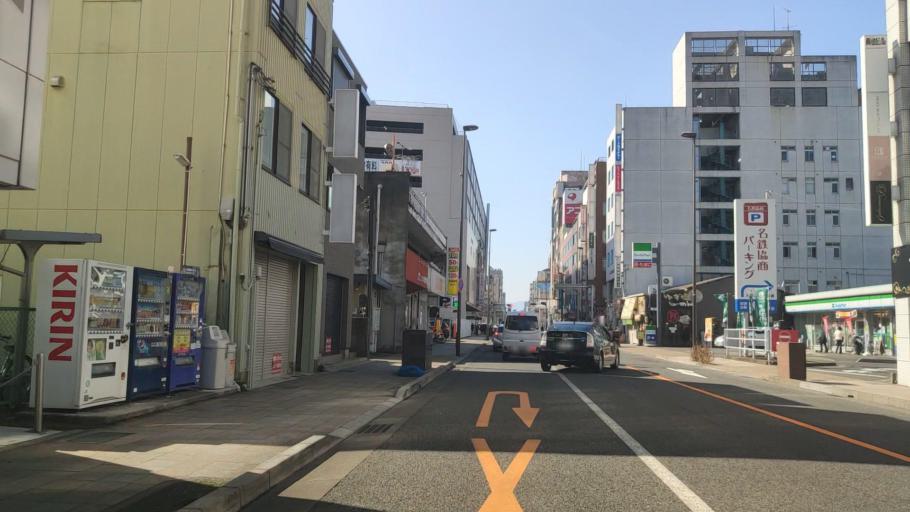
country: JP
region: Gifu
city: Gifu-shi
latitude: 35.4121
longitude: 136.7617
